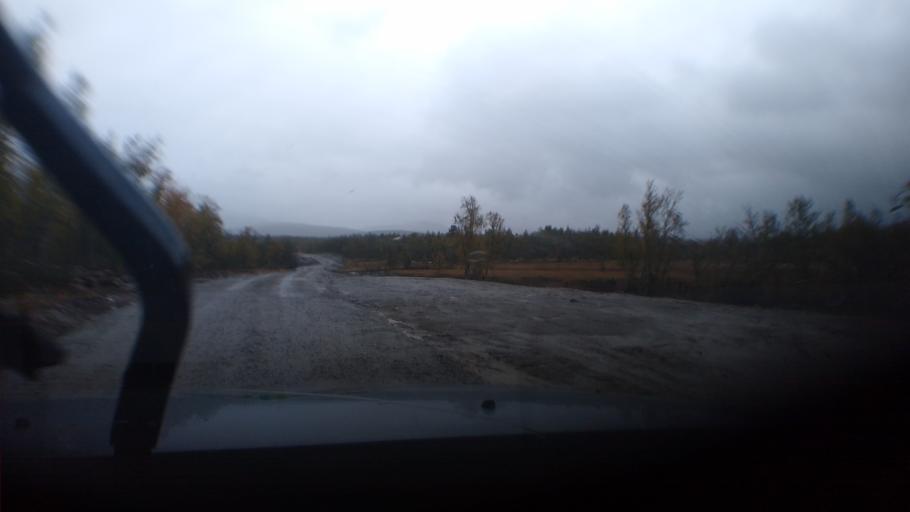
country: NO
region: Oppland
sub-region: Ringebu
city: Ringebu
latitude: 61.6551
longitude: 10.1029
